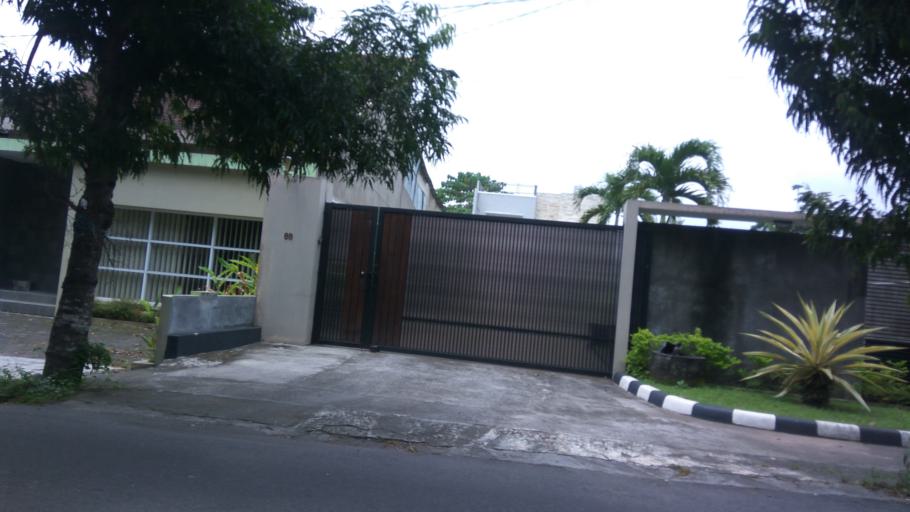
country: ID
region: Daerah Istimewa Yogyakarta
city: Melati
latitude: -7.7225
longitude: 110.3822
